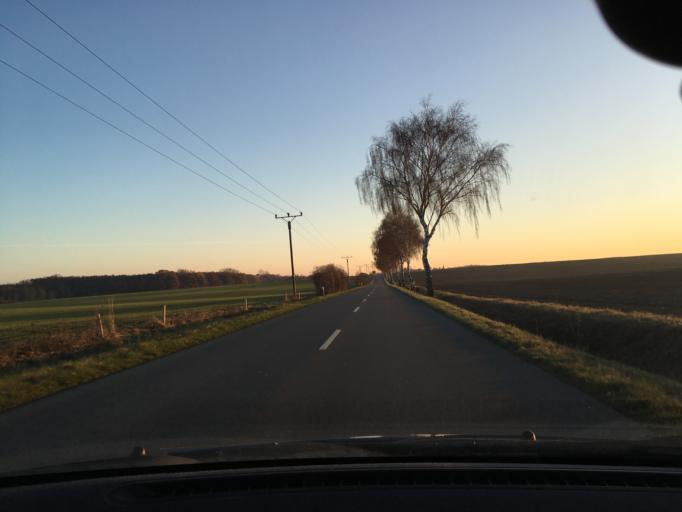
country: DE
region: Lower Saxony
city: Natendorf
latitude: 53.0941
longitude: 10.4674
